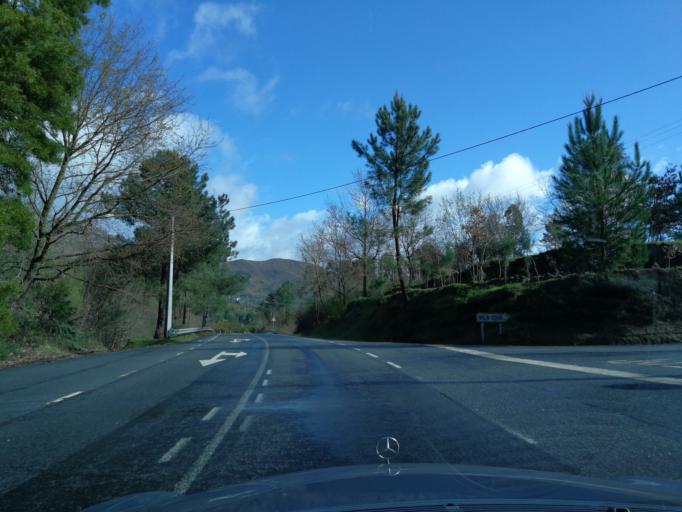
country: PT
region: Viana do Castelo
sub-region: Ponte da Barca
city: Ponte da Barca
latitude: 41.8108
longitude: -8.3414
